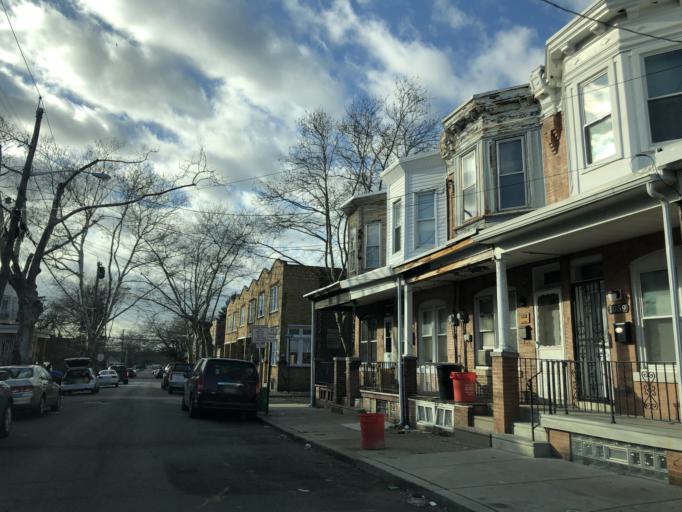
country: US
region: New Jersey
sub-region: Camden County
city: Camden
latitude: 39.9264
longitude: -75.1081
